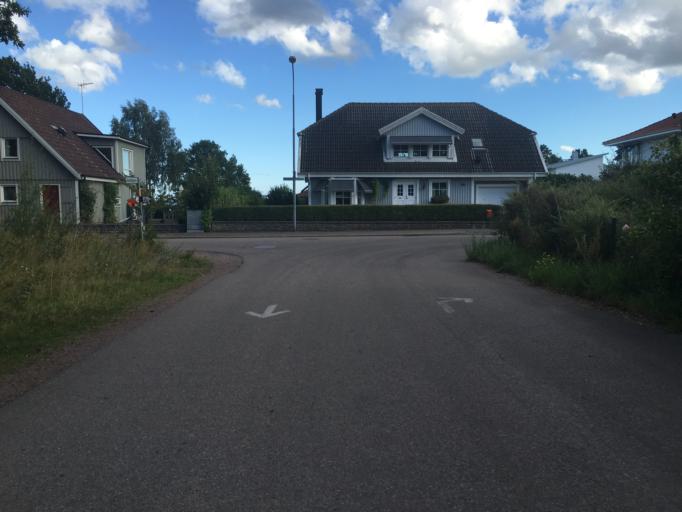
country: SE
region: Kalmar
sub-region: Kalmar Kommun
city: Kalmar
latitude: 56.7017
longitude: 16.3730
